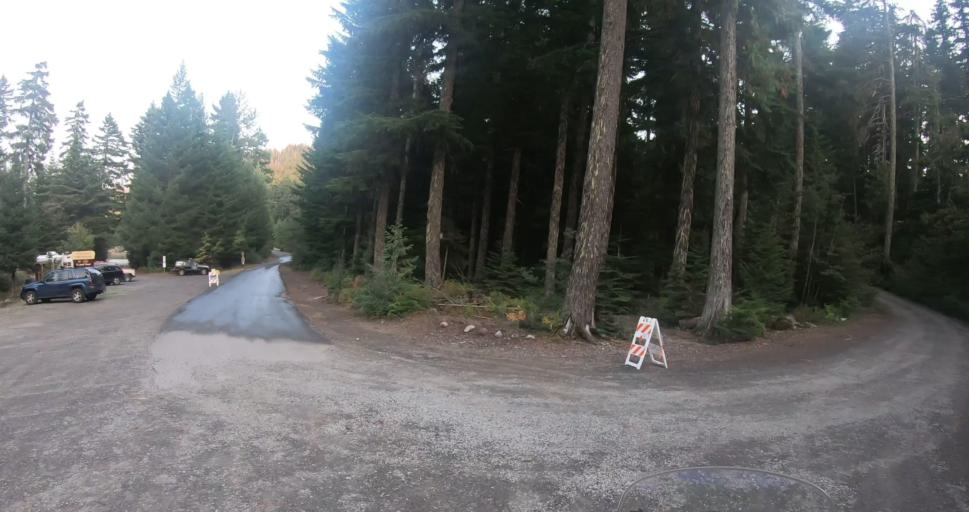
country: US
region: Oregon
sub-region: Hood River County
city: Odell
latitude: 45.4575
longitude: -121.6638
